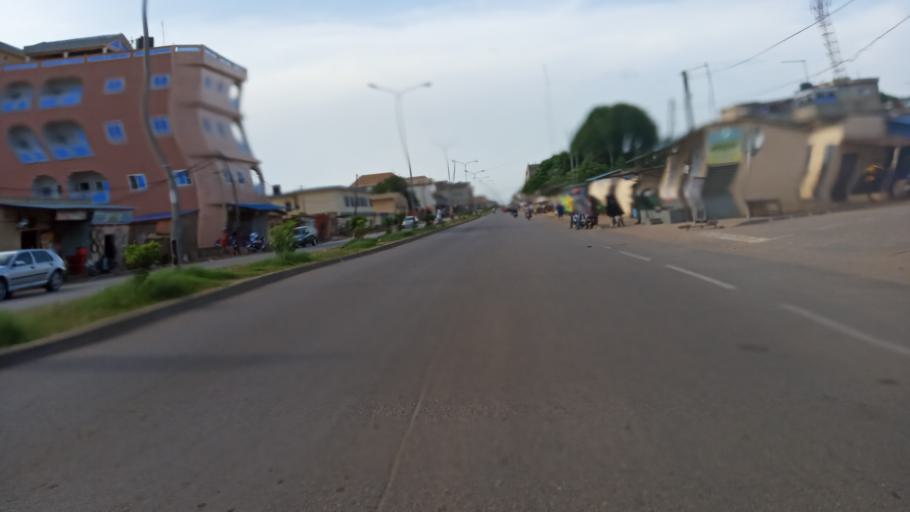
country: TG
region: Maritime
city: Lome
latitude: 6.1631
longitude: 1.2664
